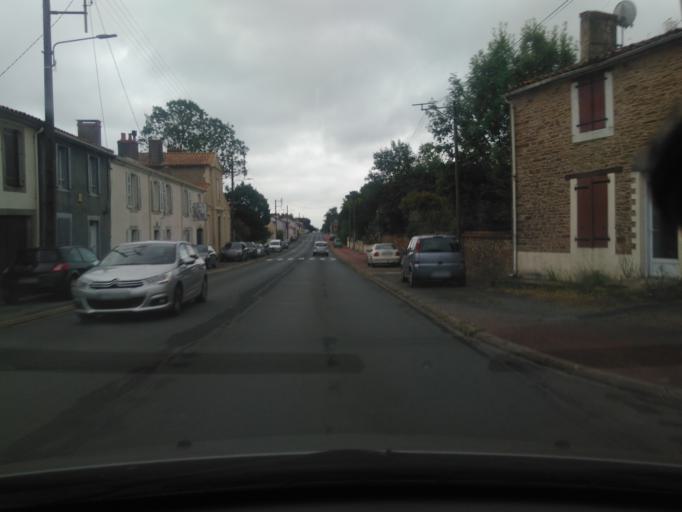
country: FR
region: Pays de la Loire
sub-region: Departement de la Vendee
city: Saint-Florent-des-Bois
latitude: 46.5917
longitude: -1.3130
